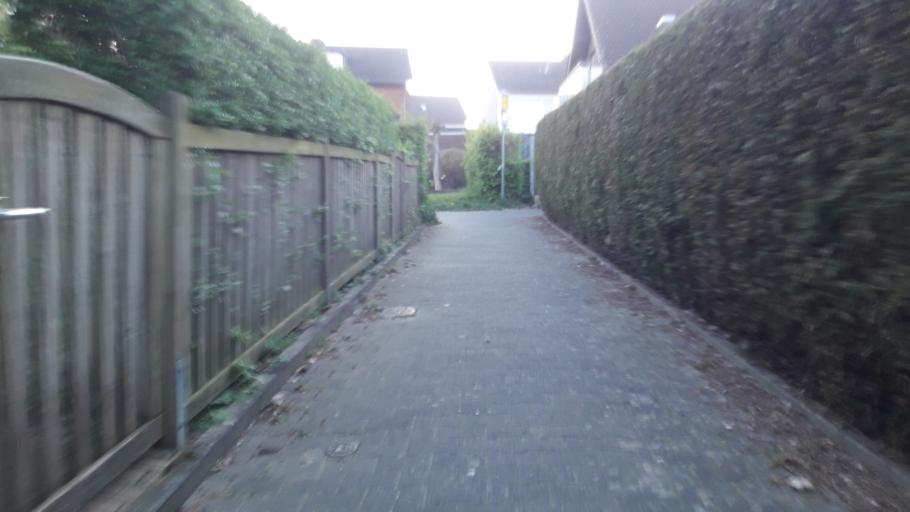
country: DE
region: North Rhine-Westphalia
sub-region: Regierungsbezirk Detmold
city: Paderborn
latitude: 51.6870
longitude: 8.6916
